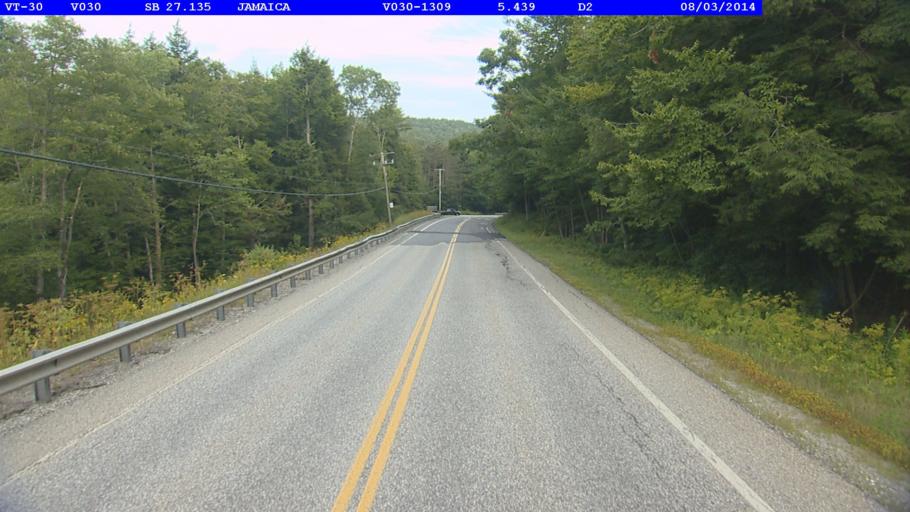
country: US
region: Vermont
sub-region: Windham County
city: Dover
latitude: 43.1118
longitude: -72.7999
